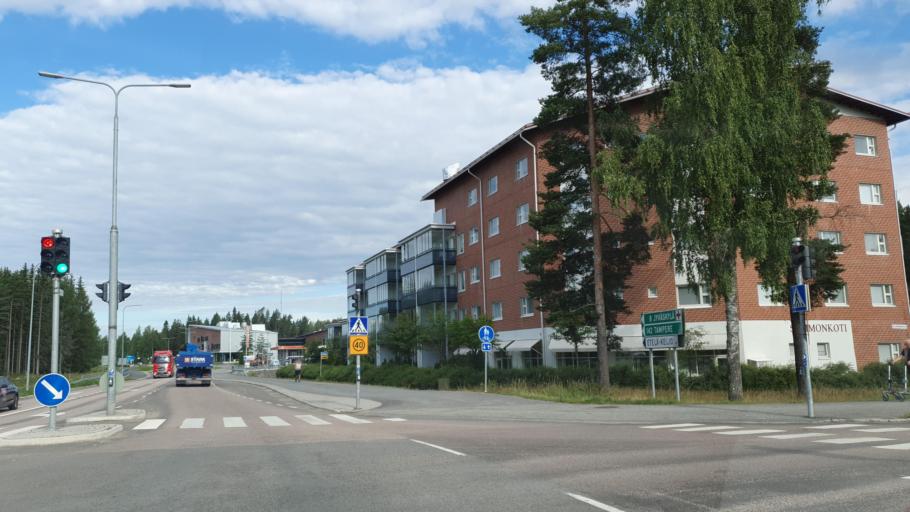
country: FI
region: Central Finland
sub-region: Jyvaeskylae
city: Jyvaeskylae
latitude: 62.1889
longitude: 25.7132
